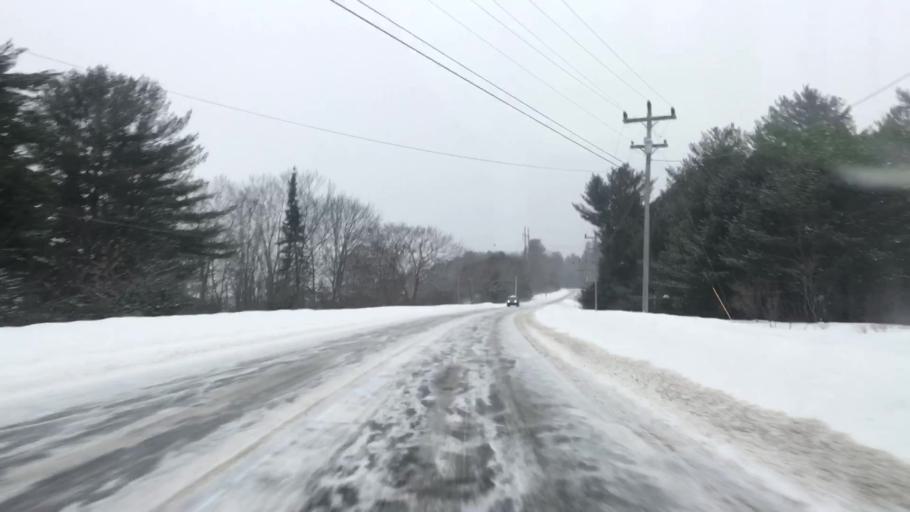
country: US
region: Maine
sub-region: Penobscot County
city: Medway
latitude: 45.5659
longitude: -68.4007
